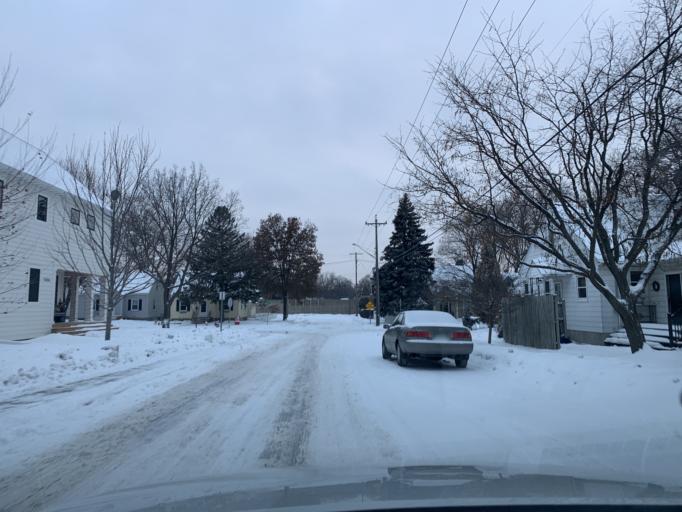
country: US
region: Minnesota
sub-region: Hennepin County
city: Saint Louis Park
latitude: 44.9273
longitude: -93.3478
